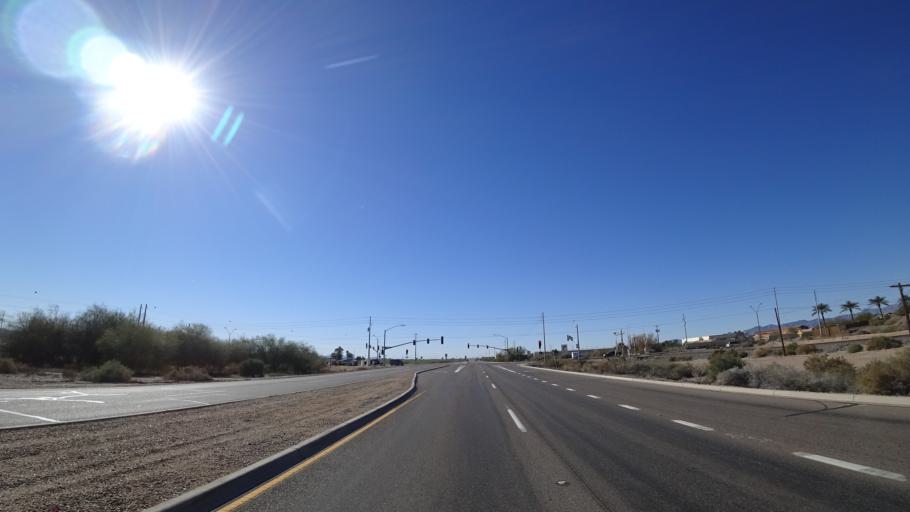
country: US
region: Arizona
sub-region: Maricopa County
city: Goodyear
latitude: 33.4089
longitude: -112.3909
